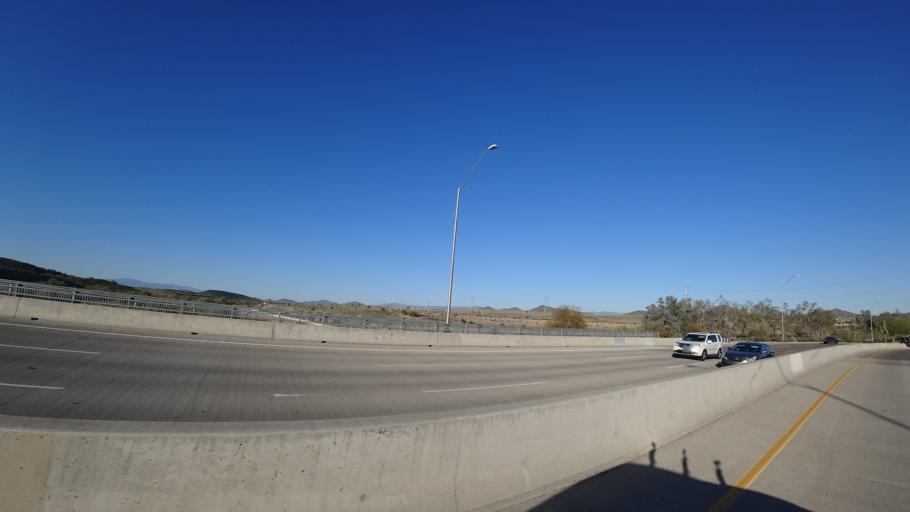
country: US
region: Arizona
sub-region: Maricopa County
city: Anthem
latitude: 33.7130
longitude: -112.1263
